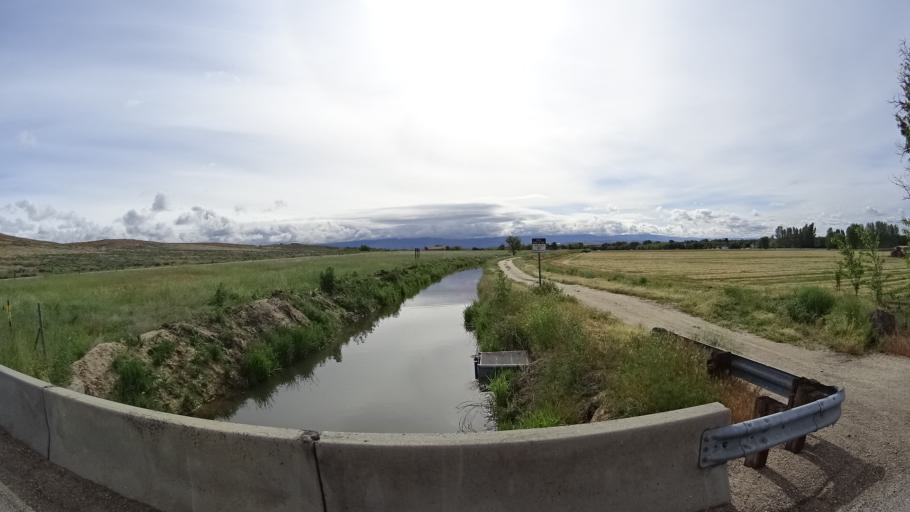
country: US
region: Idaho
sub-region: Ada County
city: Eagle
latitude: 43.7350
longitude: -116.4133
